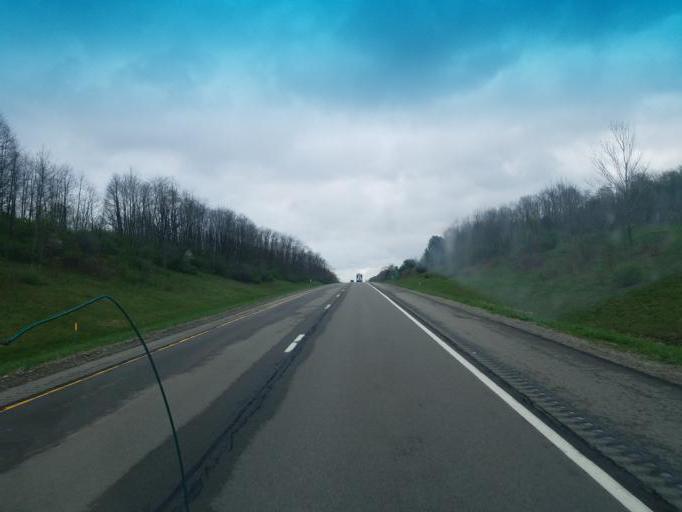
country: US
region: New York
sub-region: Chautauqua County
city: Clymer
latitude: 42.1468
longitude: -79.6410
